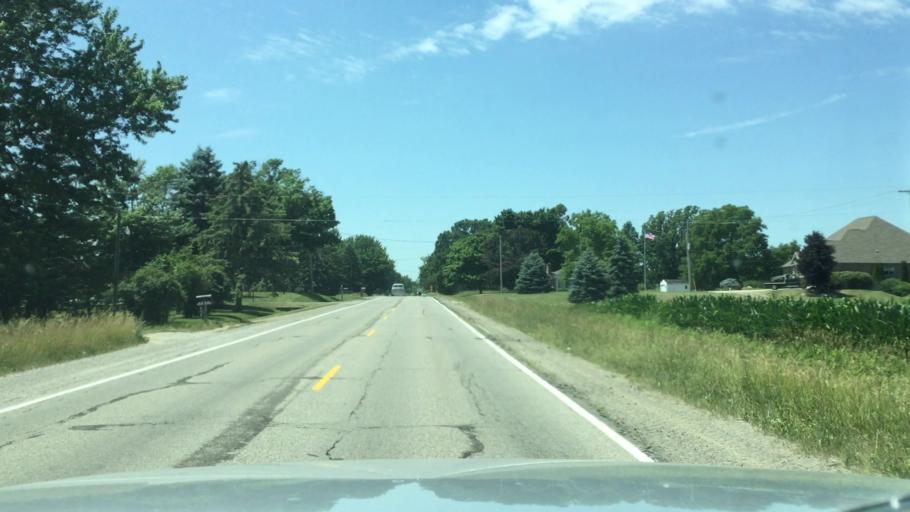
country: US
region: Michigan
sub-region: Genesee County
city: Swartz Creek
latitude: 42.9428
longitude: -83.8029
